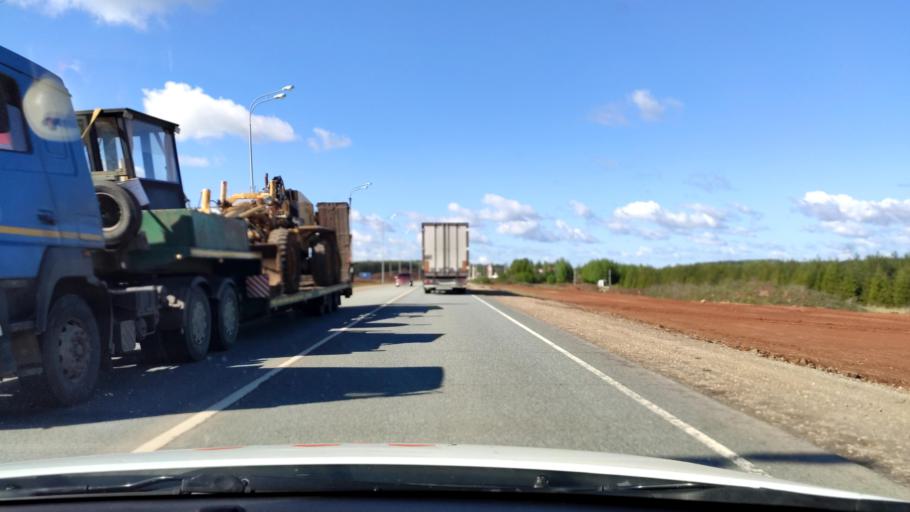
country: RU
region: Tatarstan
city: Sviyazhsk
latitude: 55.7352
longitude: 48.7797
